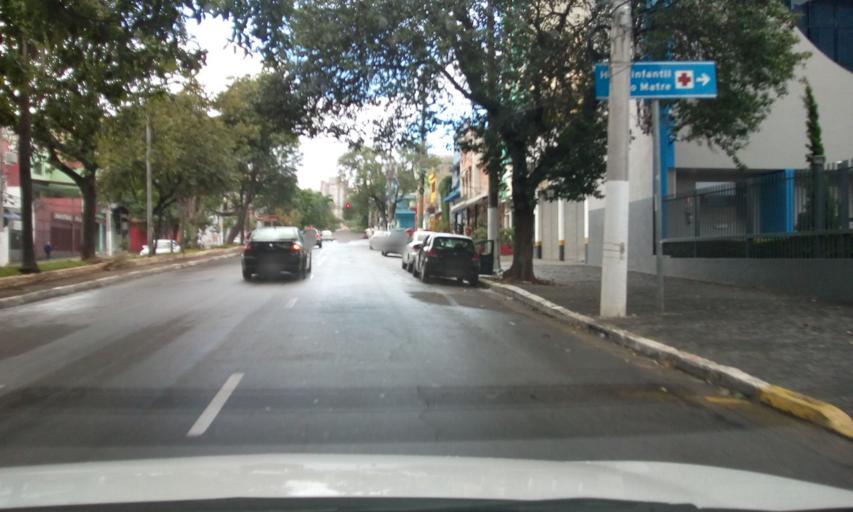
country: BR
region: Sao Paulo
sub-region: Sao Paulo
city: Sao Paulo
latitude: -23.5566
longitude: -46.6456
